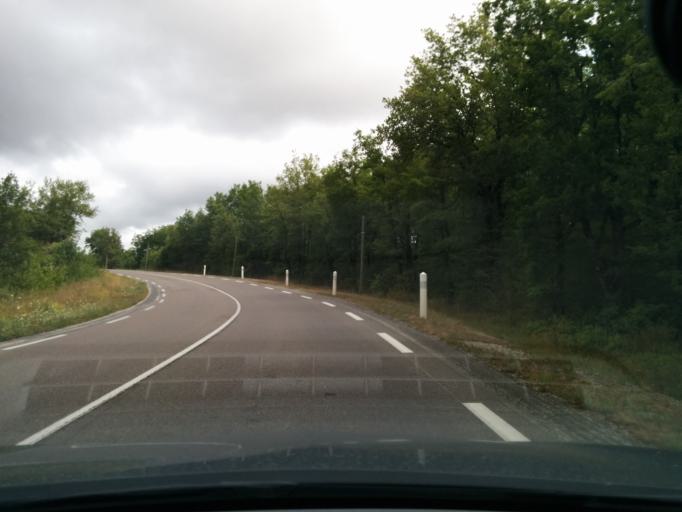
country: FR
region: Midi-Pyrenees
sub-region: Departement du Lot
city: Souillac
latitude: 44.9763
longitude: 1.5079
